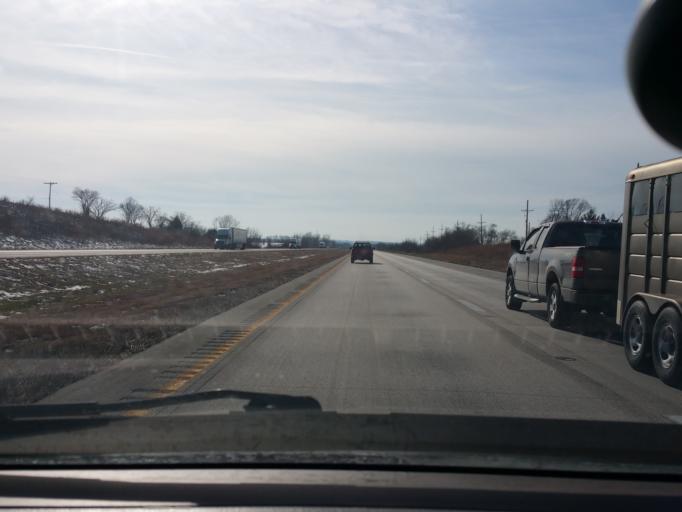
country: US
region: Missouri
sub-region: Clay County
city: Kearney
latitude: 39.4297
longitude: -94.3387
